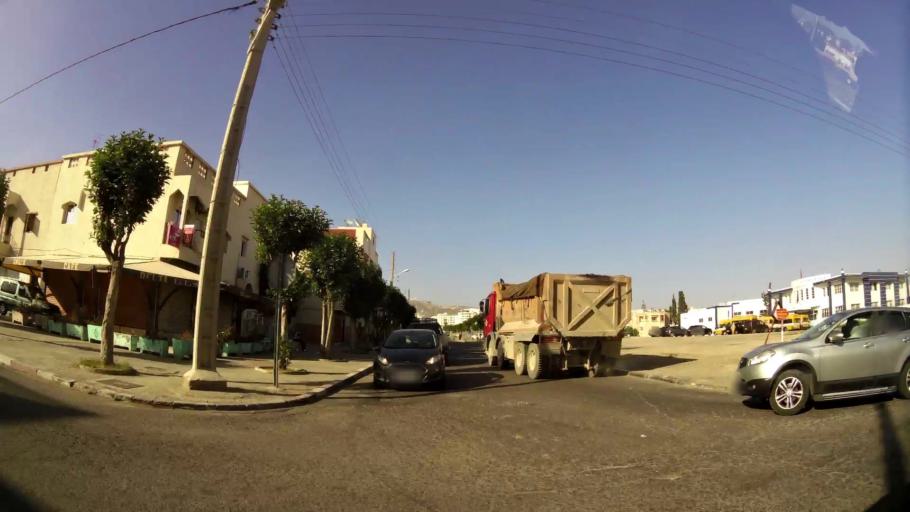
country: MA
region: Souss-Massa-Draa
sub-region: Agadir-Ida-ou-Tnan
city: Agadir
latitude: 30.4296
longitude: -9.5747
